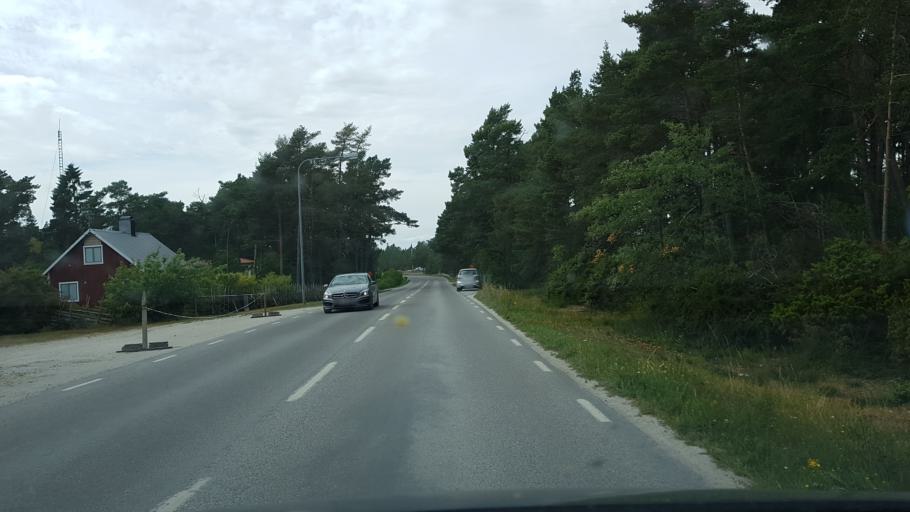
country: SE
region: Gotland
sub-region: Gotland
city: Hemse
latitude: 57.3395
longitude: 18.6960
